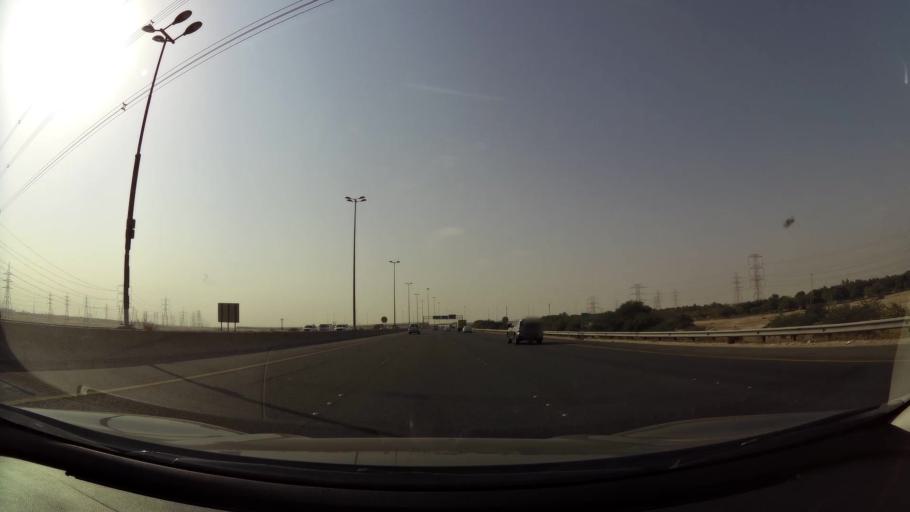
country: KW
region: Al Ahmadi
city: Al Ahmadi
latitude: 29.0717
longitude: 48.0993
